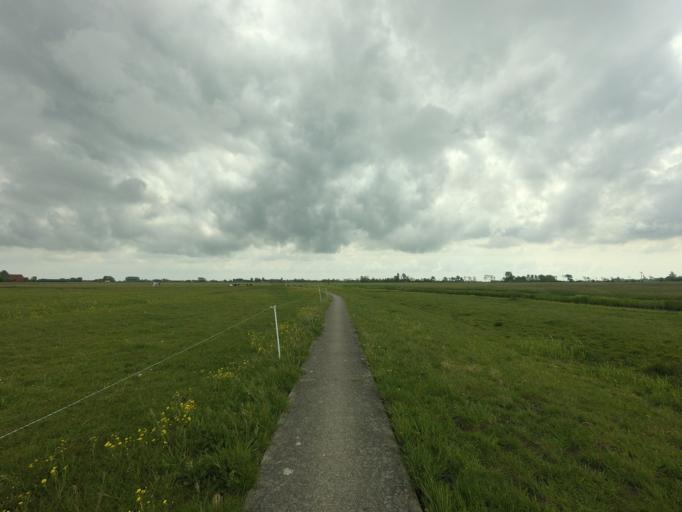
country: NL
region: Friesland
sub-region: Gemeente Littenseradiel
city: Wommels
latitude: 53.1110
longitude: 5.6030
